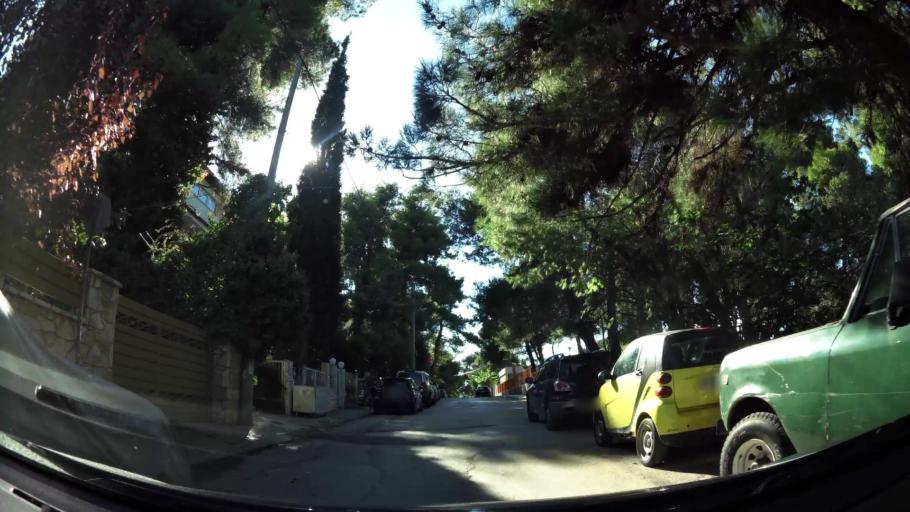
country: GR
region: Attica
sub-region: Nomarchia Anatolikis Attikis
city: Drosia
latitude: 38.1163
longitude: 23.8648
